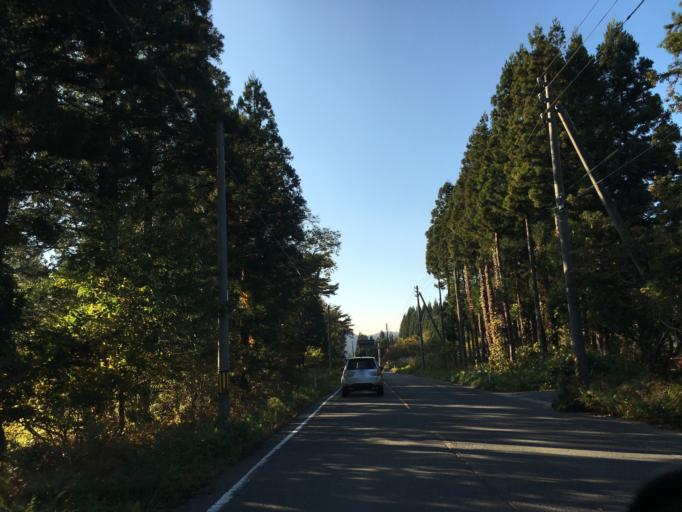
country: JP
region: Fukushima
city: Inawashiro
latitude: 37.3999
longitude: 140.1533
